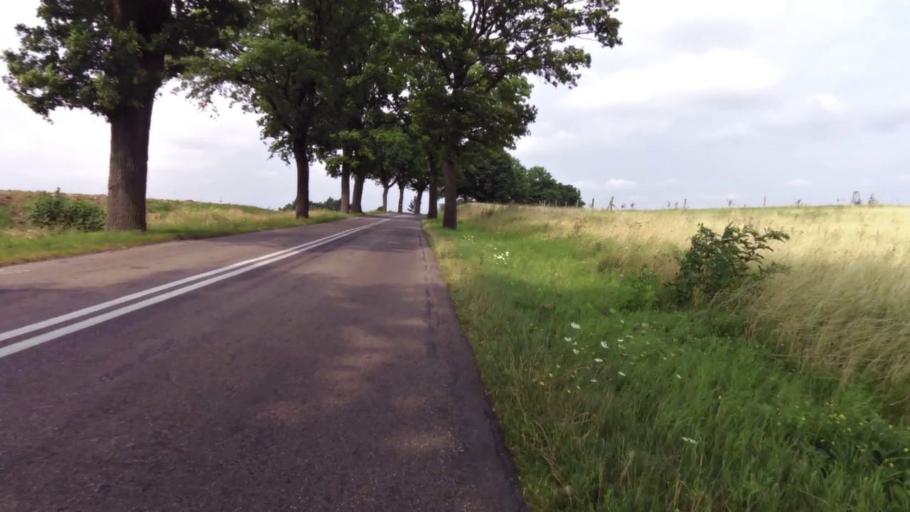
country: PL
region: West Pomeranian Voivodeship
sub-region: Powiat drawski
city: Drawsko Pomorskie
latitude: 53.5608
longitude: 15.8287
